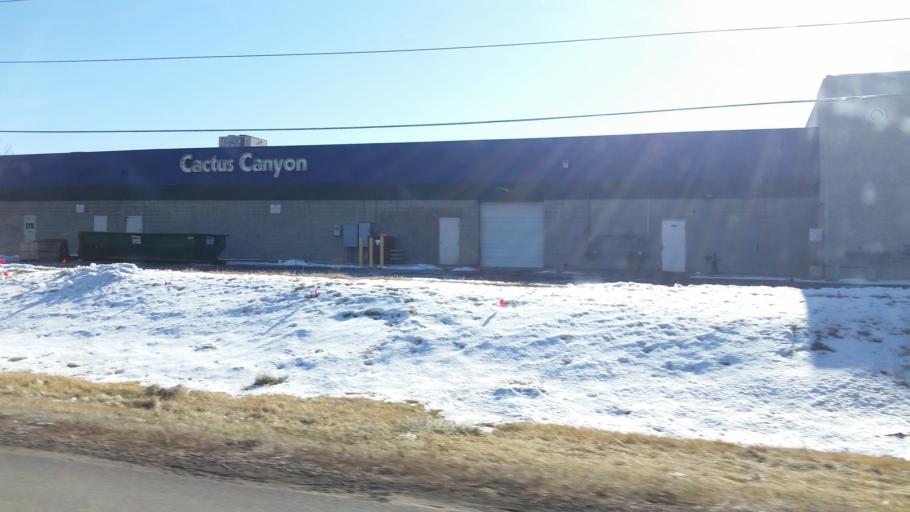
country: US
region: Colorado
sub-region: Weld County
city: Evans
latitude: 40.3919
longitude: -104.7083
